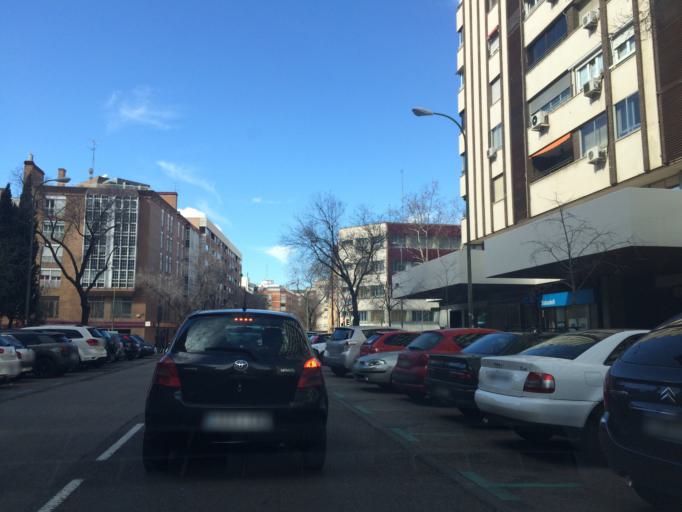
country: ES
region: Madrid
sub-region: Provincia de Madrid
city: Chamartin
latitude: 40.4609
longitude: -3.6934
